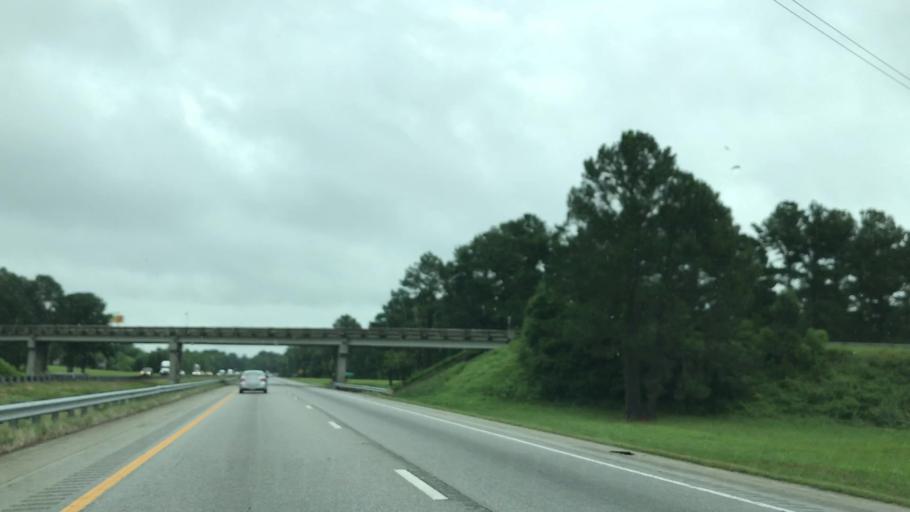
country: US
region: North Carolina
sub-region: Halifax County
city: Roanoke Rapids
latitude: 36.4676
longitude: -77.6115
